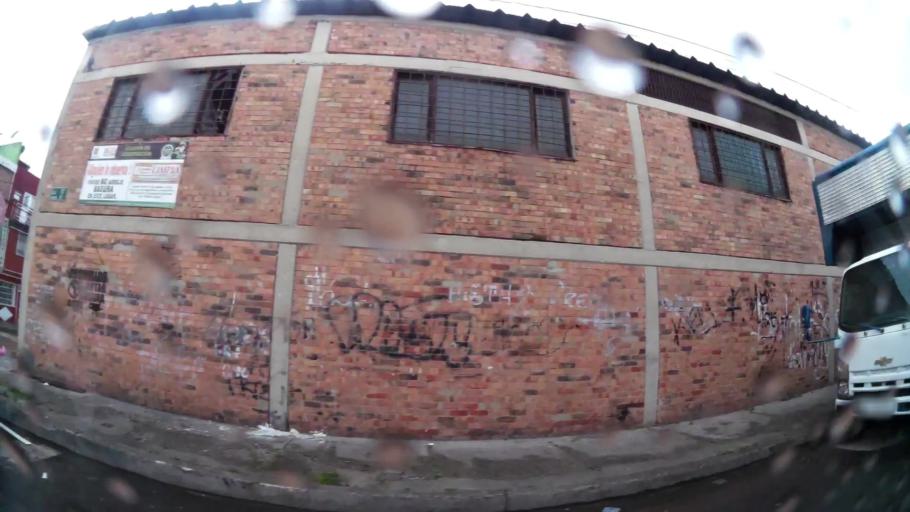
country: CO
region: Bogota D.C.
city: Barrio San Luis
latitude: 4.6768
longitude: -74.0820
